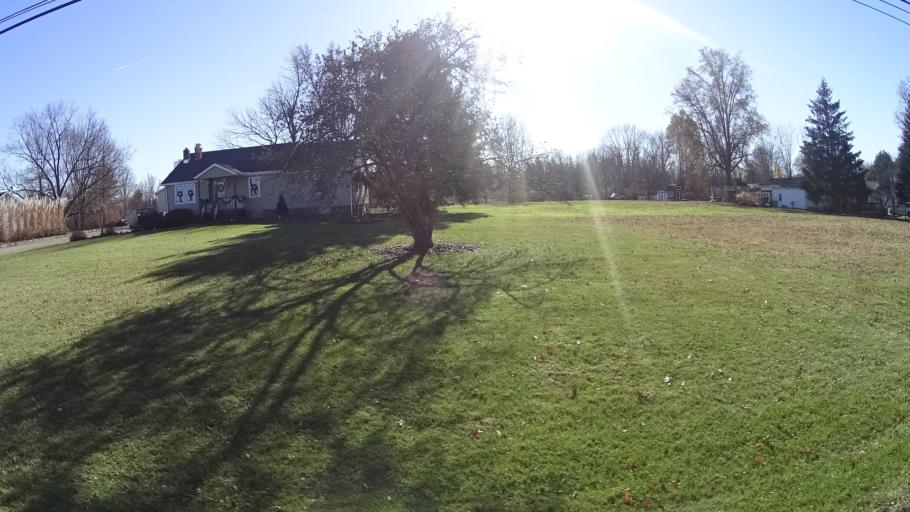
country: US
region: Ohio
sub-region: Lorain County
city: Lagrange
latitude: 41.2747
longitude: -82.1141
